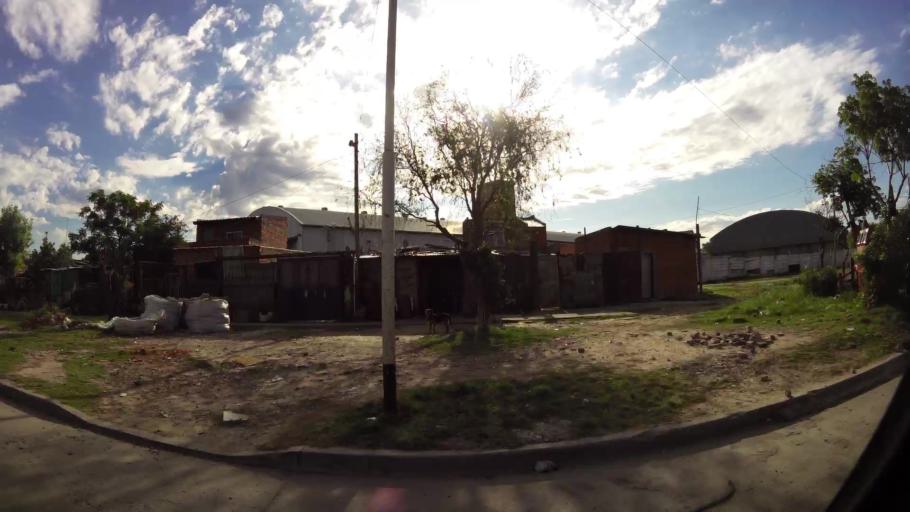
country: AR
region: Buenos Aires
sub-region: Partido de Lanus
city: Lanus
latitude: -34.7005
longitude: -58.3584
